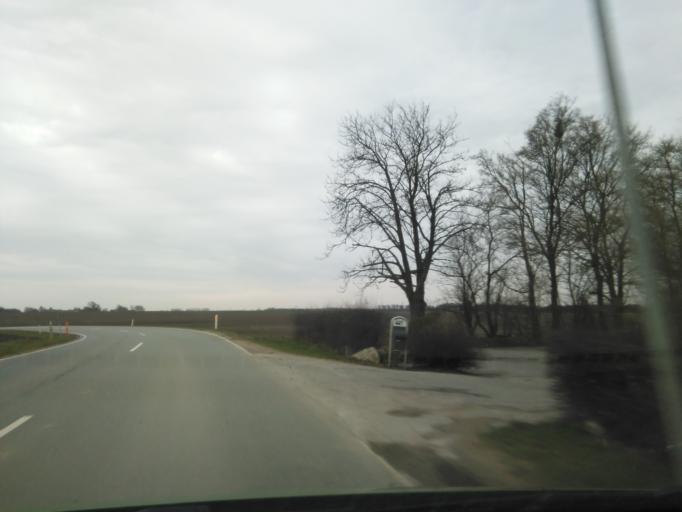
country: DK
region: Central Jutland
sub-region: Randers Kommune
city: Spentrup
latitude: 56.5470
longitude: 10.0008
